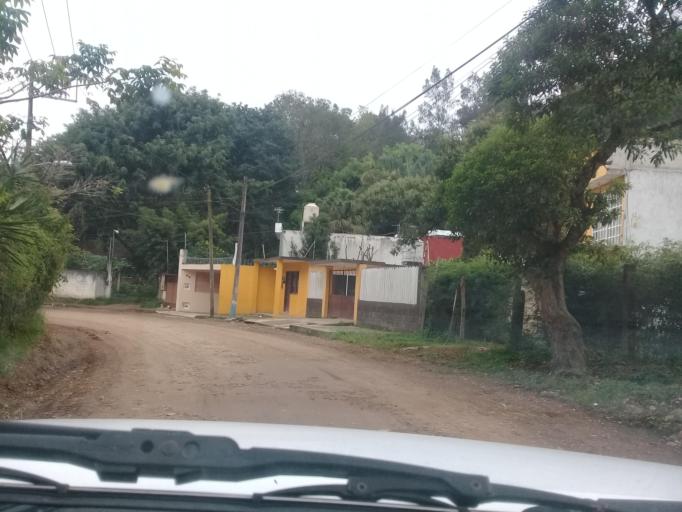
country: MX
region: Veracruz
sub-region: Xalapa
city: Lomas Verdes
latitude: 19.5065
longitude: -96.9083
